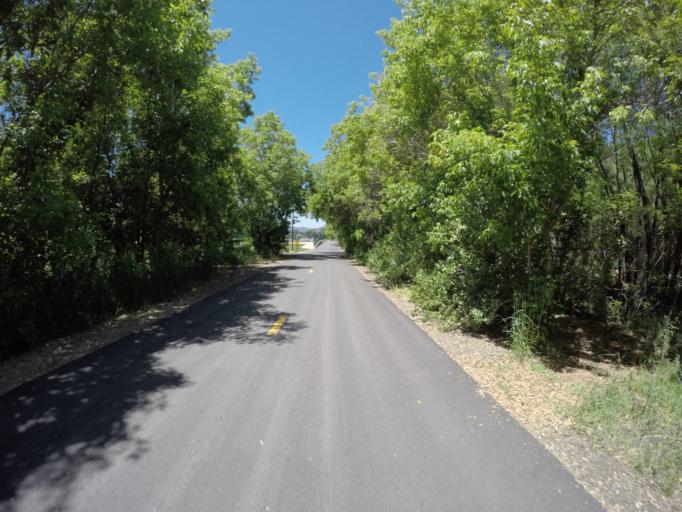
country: US
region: Utah
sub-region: Summit County
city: Park City
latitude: 40.6512
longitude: -111.5009
